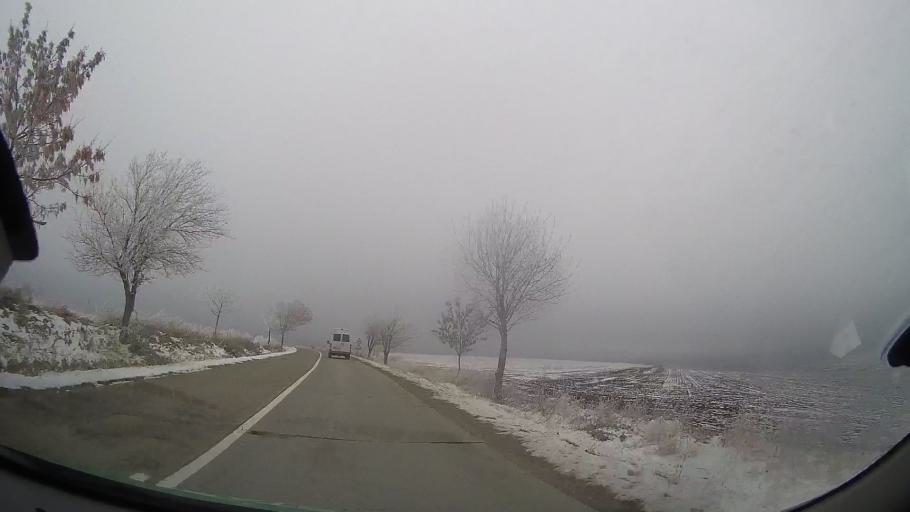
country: RO
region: Vaslui
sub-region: Comuna Ivesti
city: Ivesti
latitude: 46.1961
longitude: 27.5975
